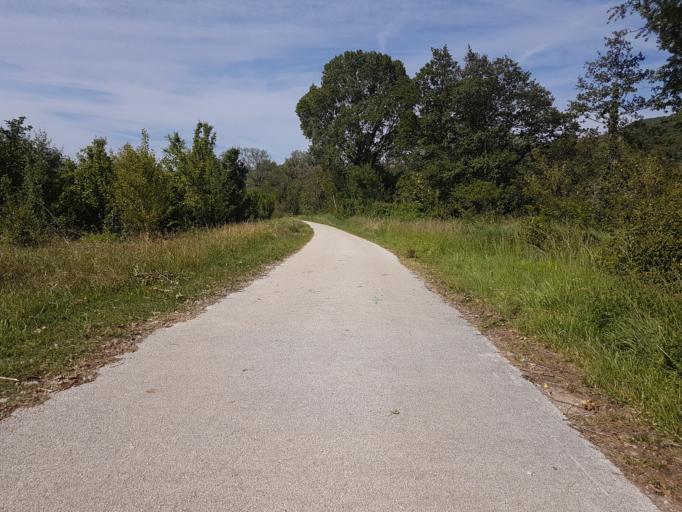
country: FR
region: Rhone-Alpes
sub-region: Departement de l'Ardeche
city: La Voulte-sur-Rhone
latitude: 44.7799
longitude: 4.7719
